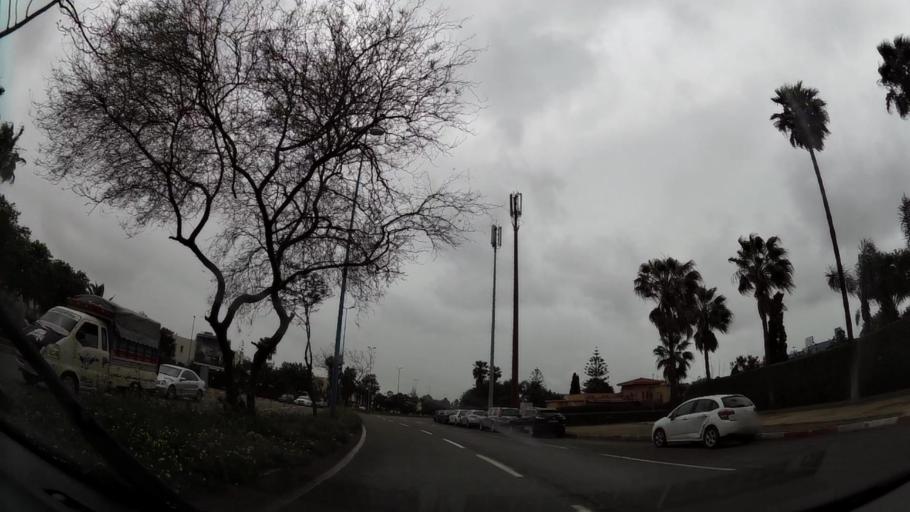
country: MA
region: Grand Casablanca
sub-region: Casablanca
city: Casablanca
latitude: 33.5308
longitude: -7.6217
